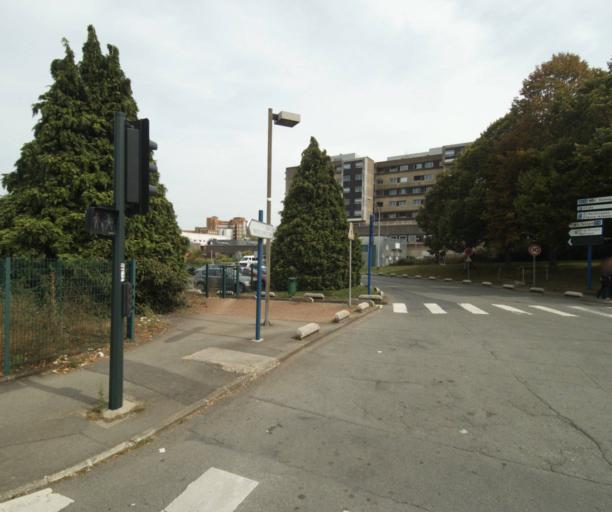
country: FR
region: Nord-Pas-de-Calais
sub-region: Departement du Nord
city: Loos
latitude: 50.6074
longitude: 3.0305
